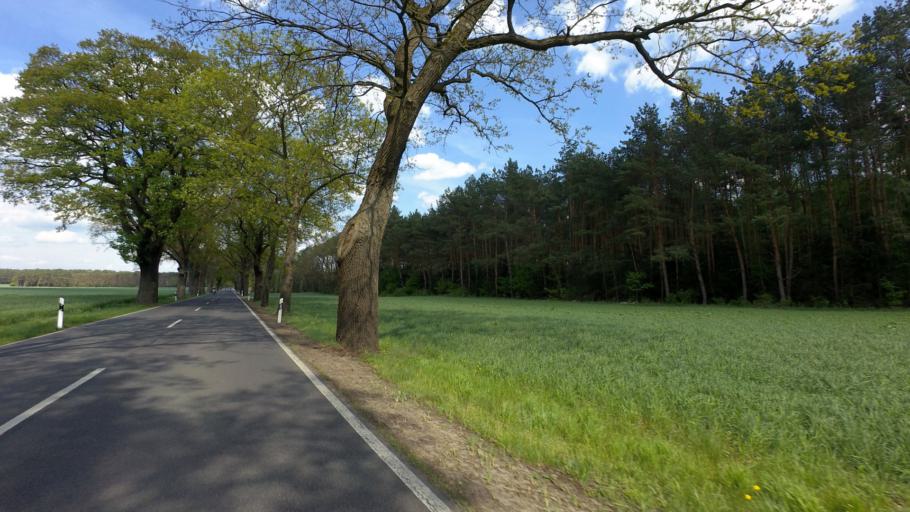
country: DE
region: Brandenburg
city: Marienwerder
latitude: 52.8737
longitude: 13.5403
